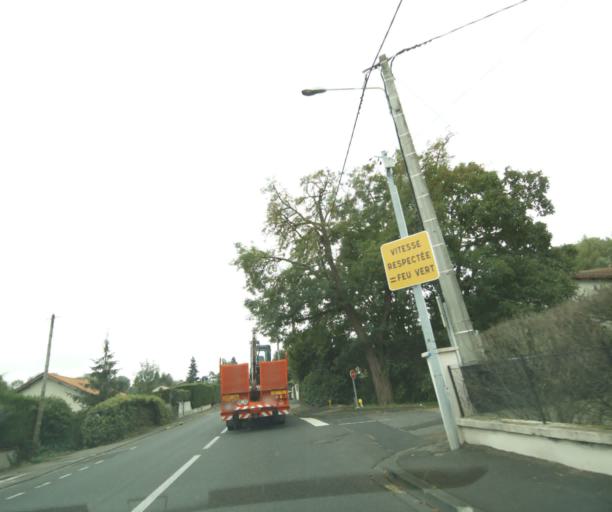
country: FR
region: Auvergne
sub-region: Departement du Puy-de-Dome
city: Ceyrat
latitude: 45.7406
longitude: 3.0593
